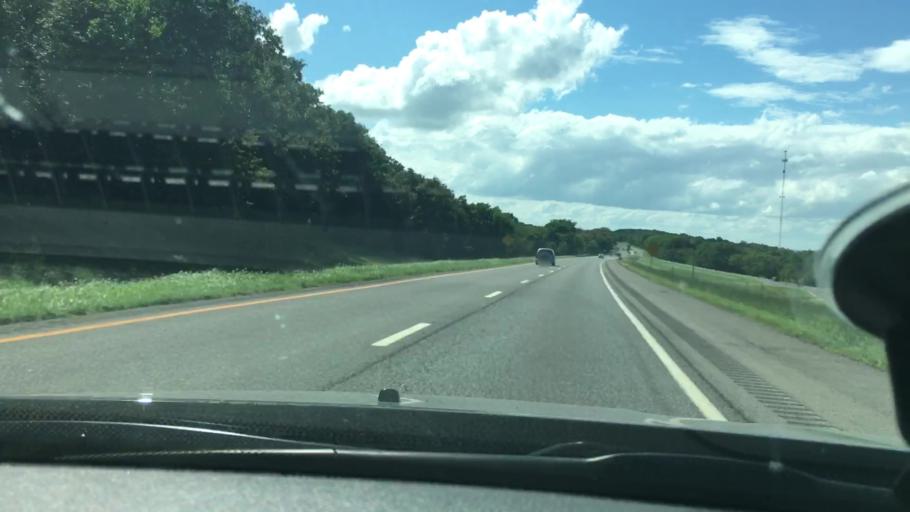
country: US
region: Oklahoma
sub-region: Sequoyah County
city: Vian
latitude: 35.4901
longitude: -95.0754
